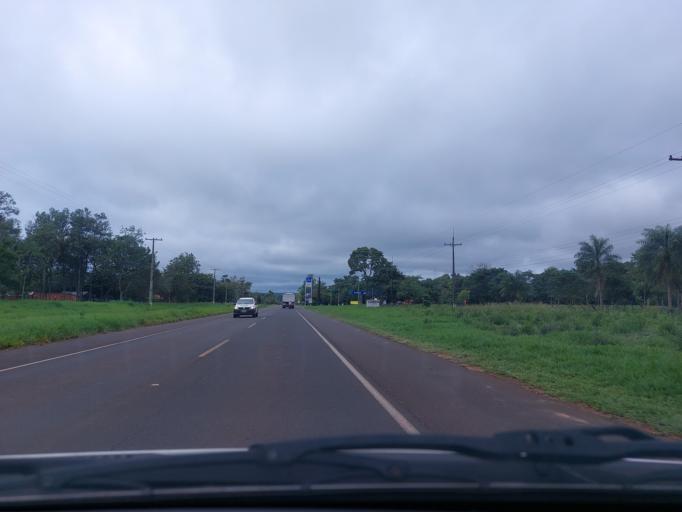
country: PY
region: San Pedro
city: Guayaybi
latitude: -24.6182
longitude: -56.3808
